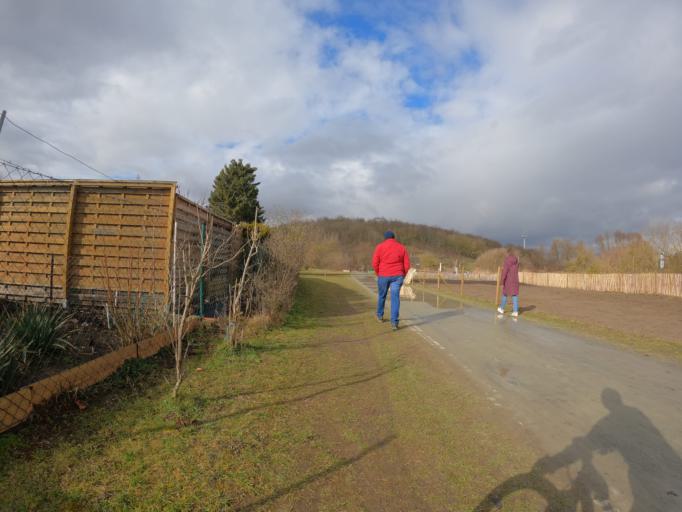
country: DE
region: Berlin
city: Kaulsdorf
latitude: 52.5302
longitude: 13.5813
